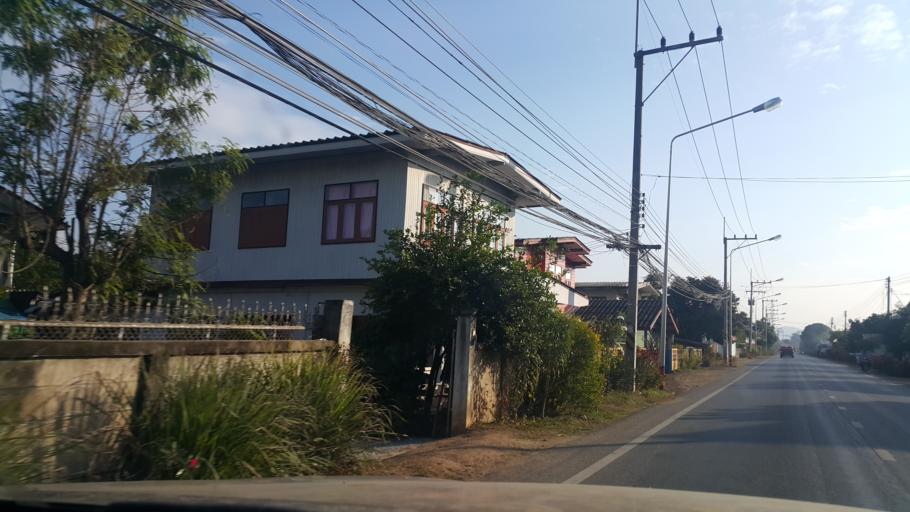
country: TH
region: Lampang
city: Ko Kha
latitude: 18.1213
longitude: 99.3464
